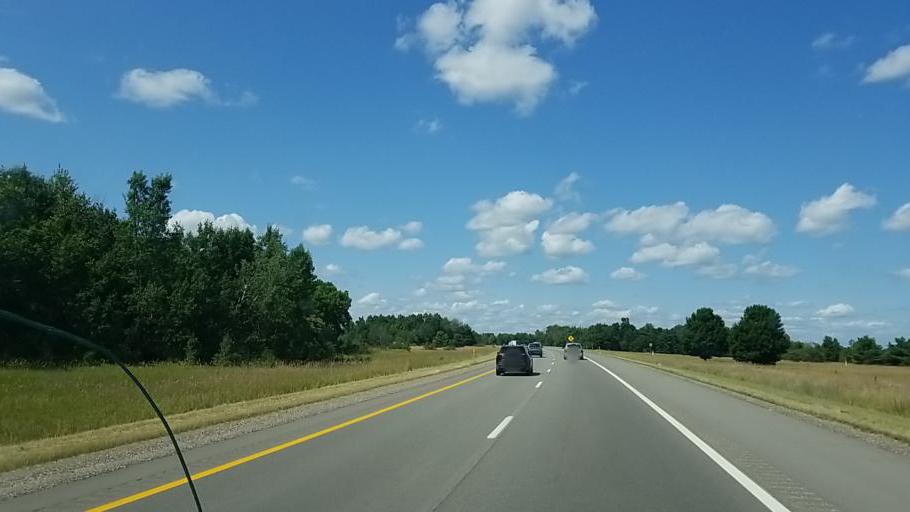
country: US
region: Michigan
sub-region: Montcalm County
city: Howard City
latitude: 43.4610
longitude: -85.4772
